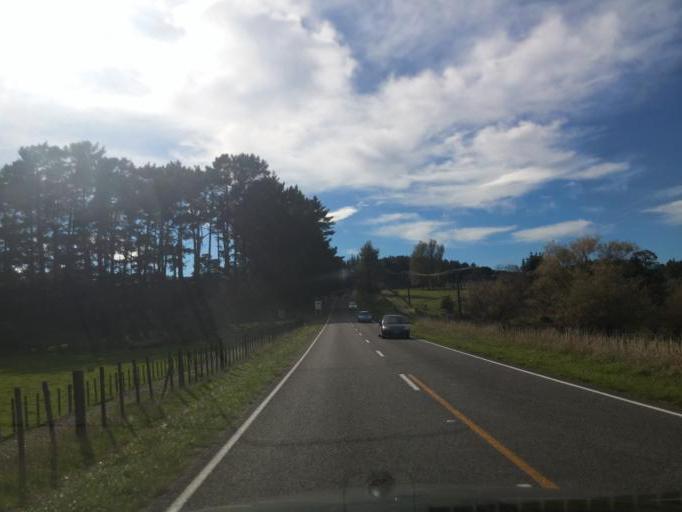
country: NZ
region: Manawatu-Wanganui
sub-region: Palmerston North City
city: Palmerston North
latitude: -40.3935
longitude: 175.6333
